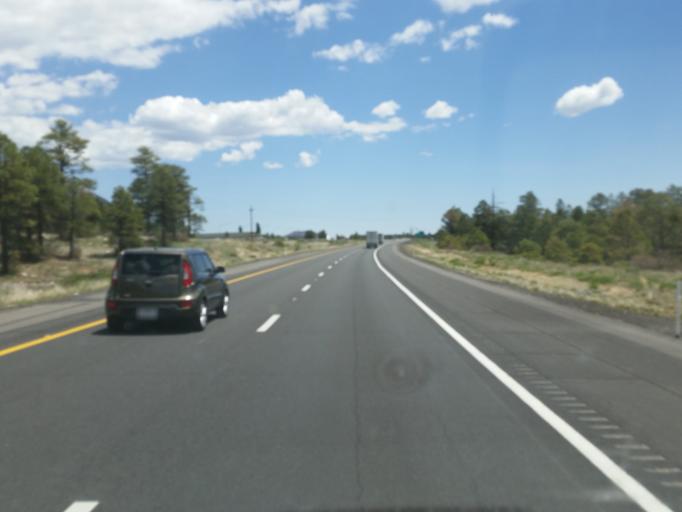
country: US
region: Arizona
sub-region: Coconino County
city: Flagstaff
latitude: 35.1867
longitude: -111.6296
